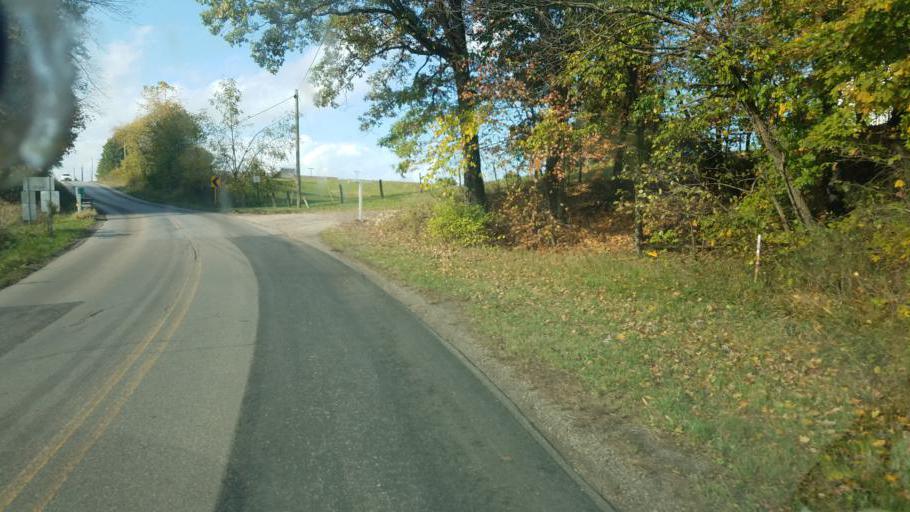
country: US
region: Ohio
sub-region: Wayne County
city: Apple Creek
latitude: 40.6670
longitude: -81.8609
